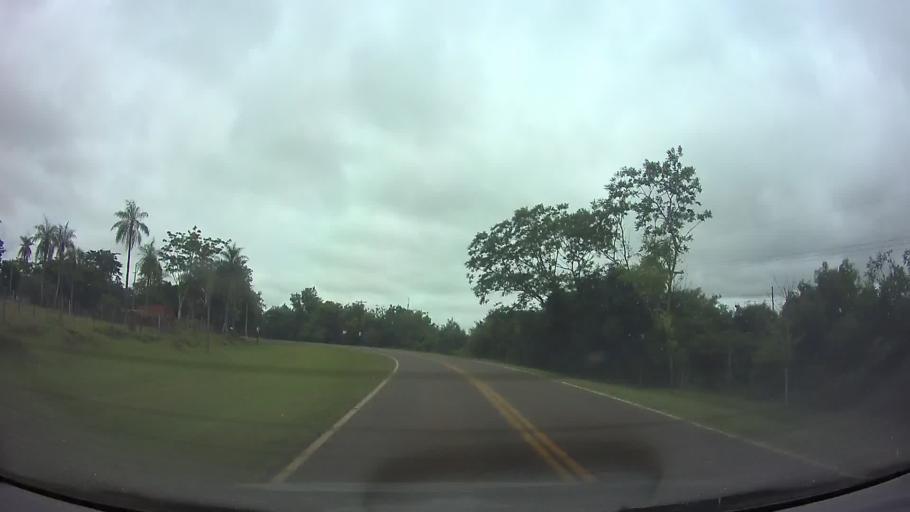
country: PY
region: Paraguari
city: Acahay
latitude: -25.9240
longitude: -57.1067
